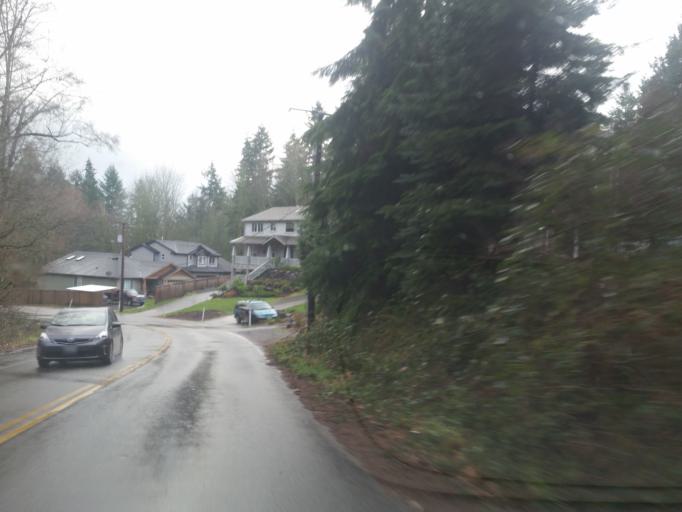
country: US
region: Washington
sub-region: Snohomish County
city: Brier
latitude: 47.7891
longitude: -122.2617
